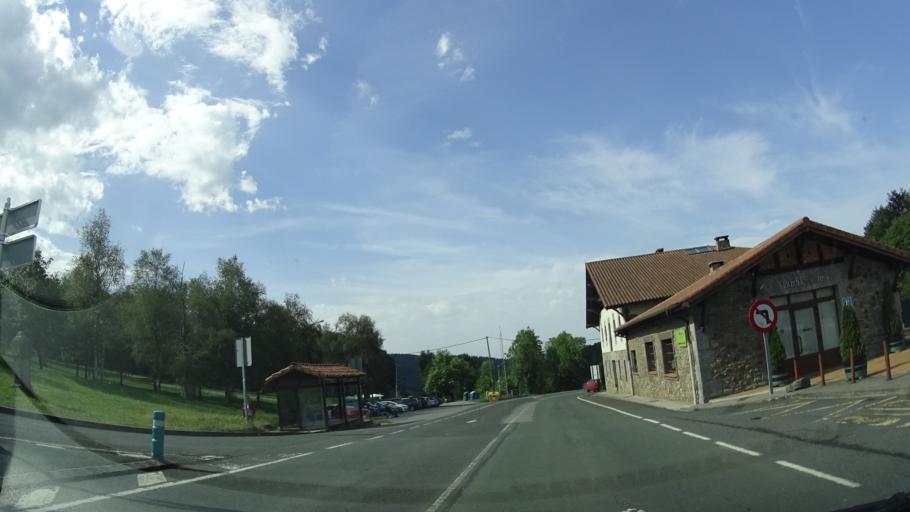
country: ES
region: Basque Country
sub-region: Bizkaia
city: Manaria
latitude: 43.1009
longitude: -2.6462
